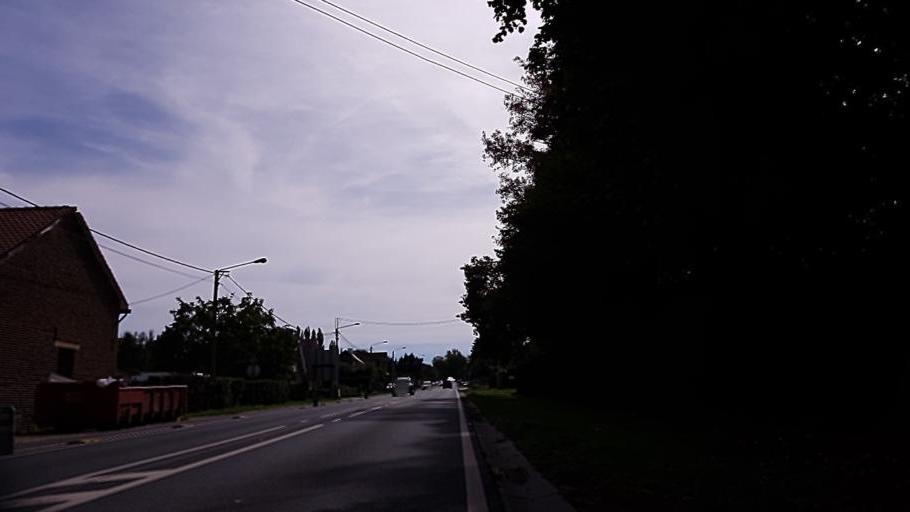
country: BE
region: Wallonia
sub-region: Province du Brabant Wallon
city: Grez-Doiceau
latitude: 50.7772
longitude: 4.7192
